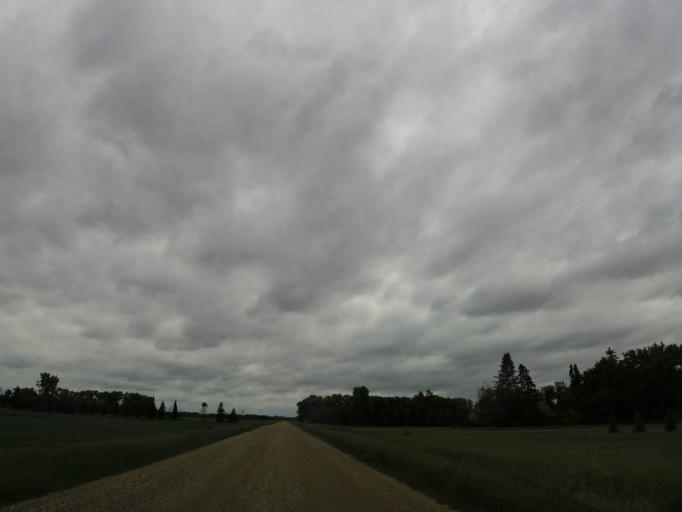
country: US
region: North Dakota
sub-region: Walsh County
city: Grafton
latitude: 48.4689
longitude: -97.5134
